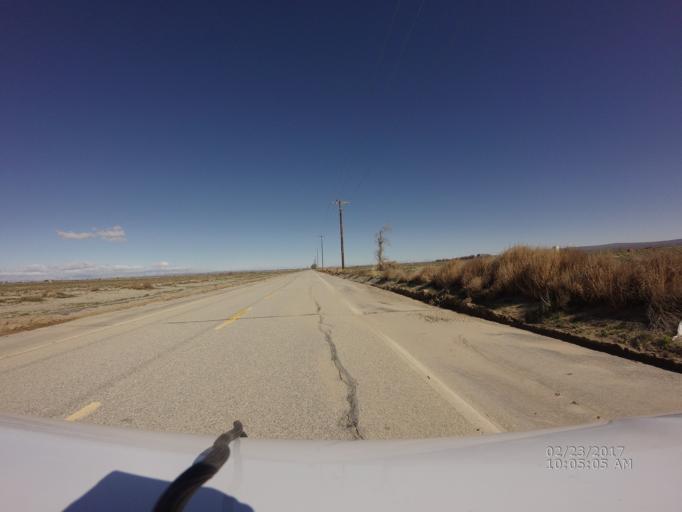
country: US
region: California
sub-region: Los Angeles County
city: Lake Los Angeles
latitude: 34.6836
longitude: -117.9342
